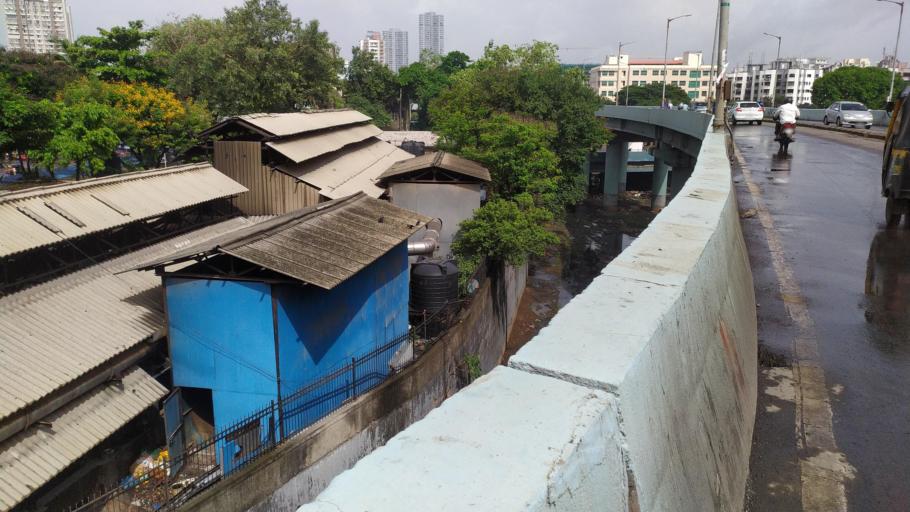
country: IN
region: Maharashtra
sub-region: Mumbai Suburban
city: Borivli
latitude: 19.2383
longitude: 72.8609
